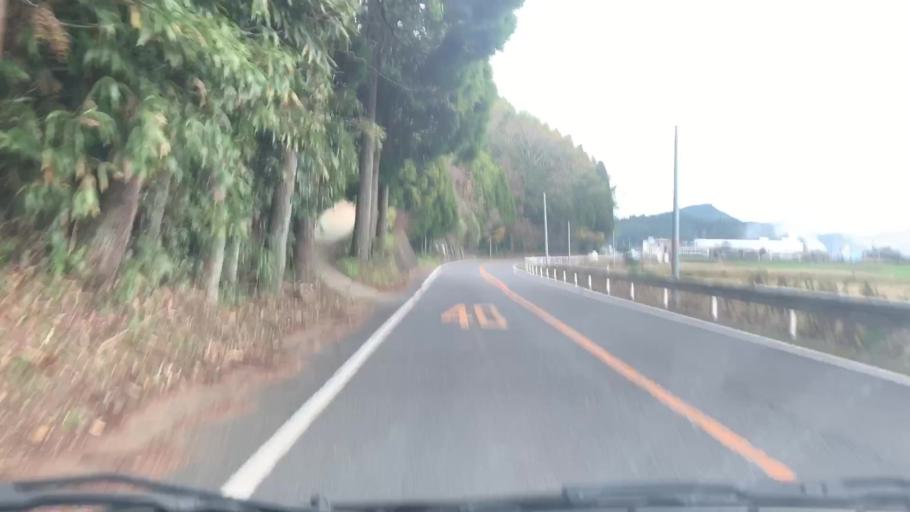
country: JP
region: Saga Prefecture
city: Takeocho-takeo
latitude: 33.2226
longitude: 129.9647
